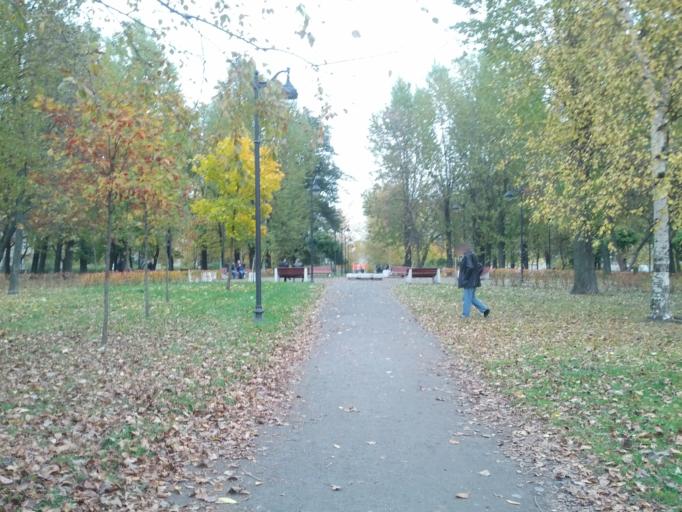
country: RU
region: St.-Petersburg
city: Obukhovo
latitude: 59.8932
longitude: 30.4164
